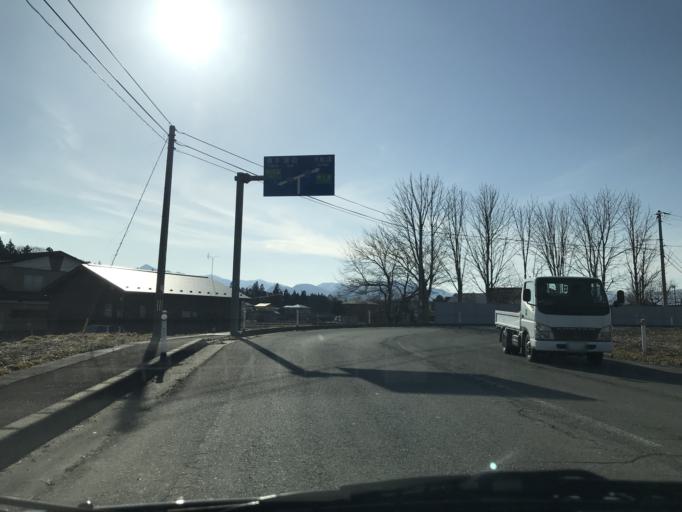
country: JP
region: Iwate
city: Kitakami
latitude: 39.3029
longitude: 141.0234
